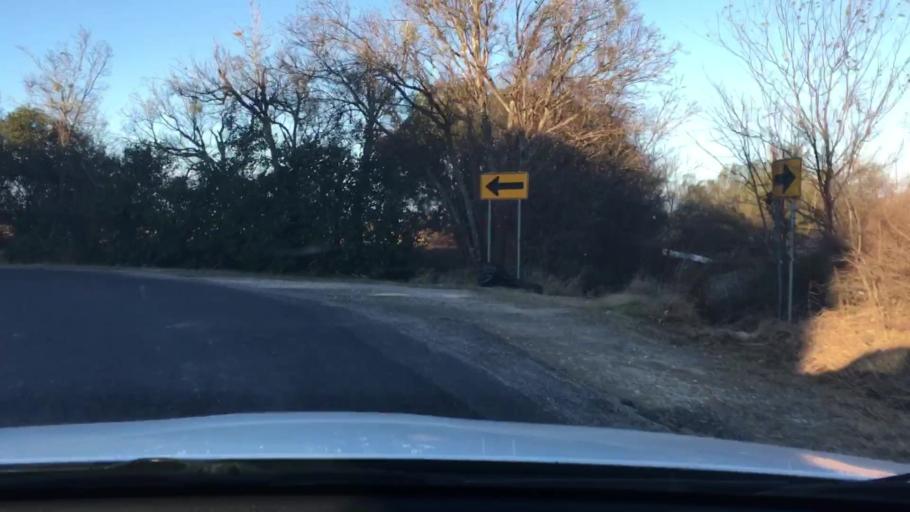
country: US
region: Texas
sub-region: Bexar County
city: Converse
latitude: 29.5260
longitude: -98.3082
